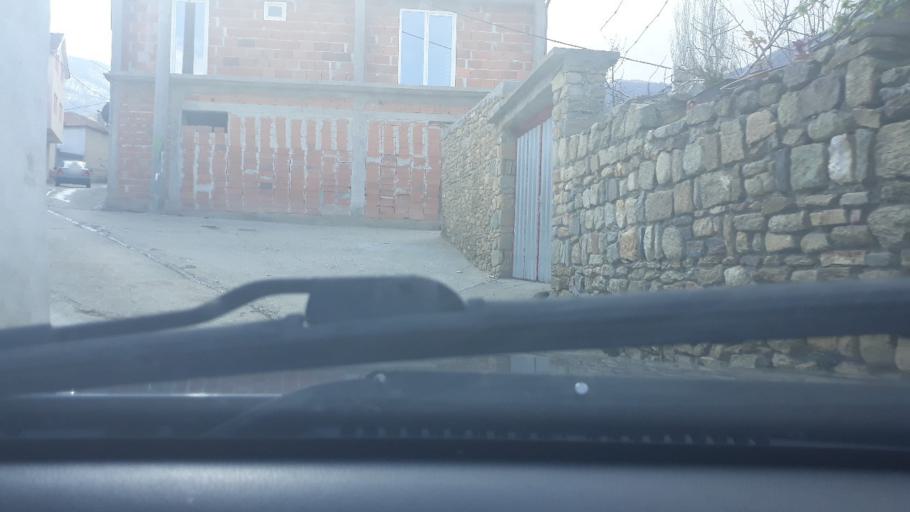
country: MK
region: Caska
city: Caska
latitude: 41.6425
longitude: 21.5909
